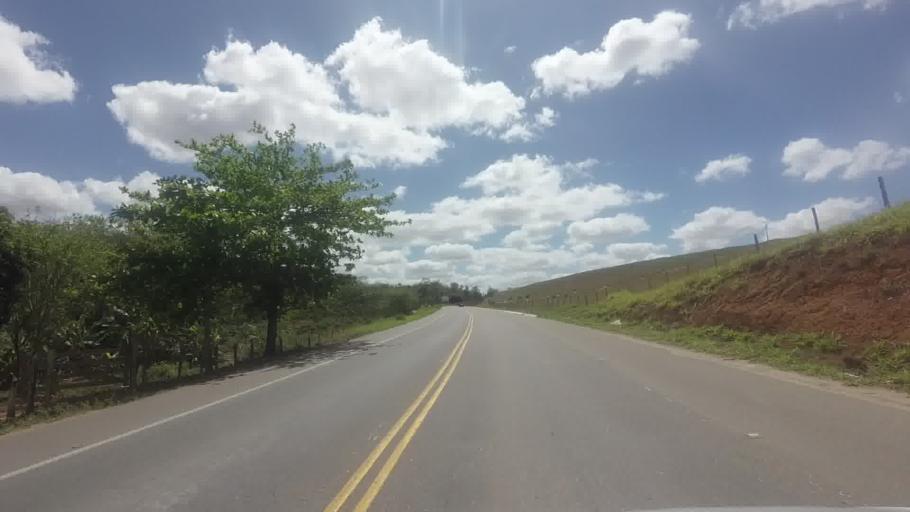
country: BR
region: Minas Gerais
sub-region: Recreio
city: Recreio
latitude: -21.6582
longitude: -42.3712
